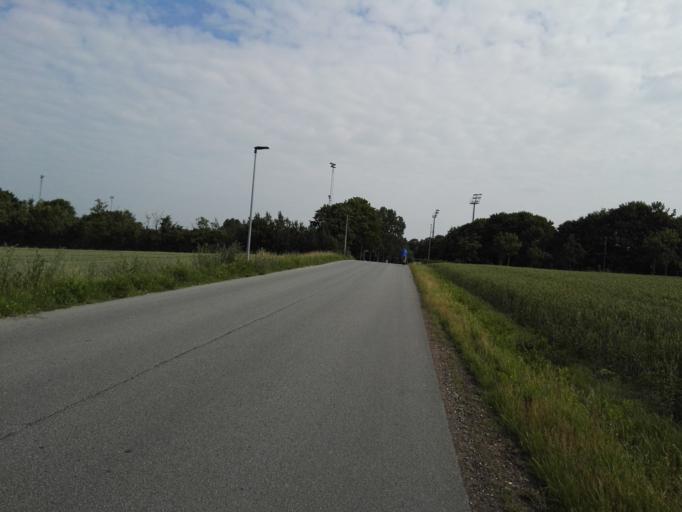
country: DK
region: Capital Region
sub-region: Egedal Kommune
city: Olstykke
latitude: 55.7808
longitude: 12.1421
